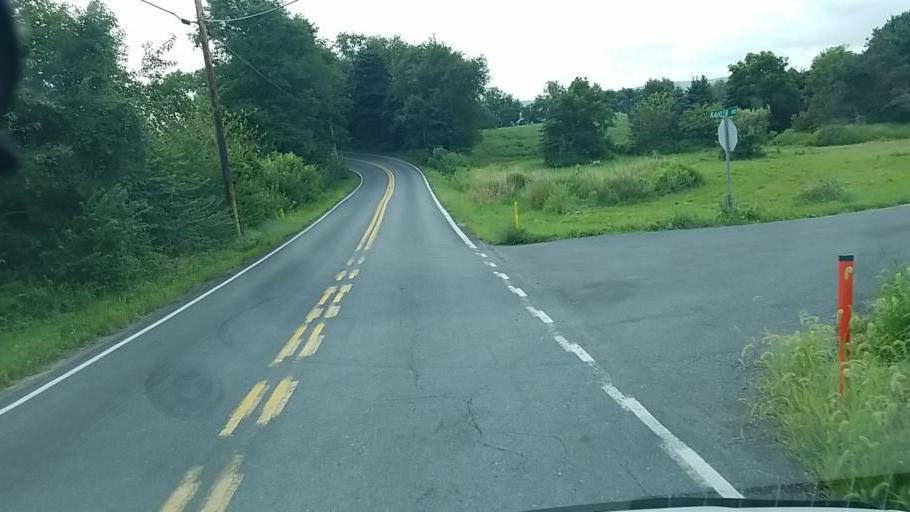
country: US
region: Pennsylvania
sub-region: Dauphin County
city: Millersburg
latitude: 40.5626
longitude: -76.8941
